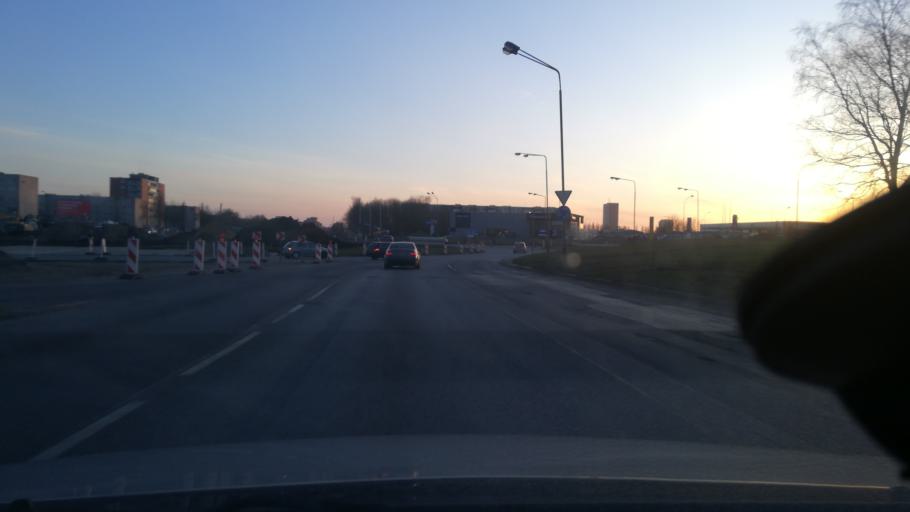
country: LT
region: Klaipedos apskritis
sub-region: Klaipeda
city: Klaipeda
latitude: 55.6911
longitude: 21.1767
